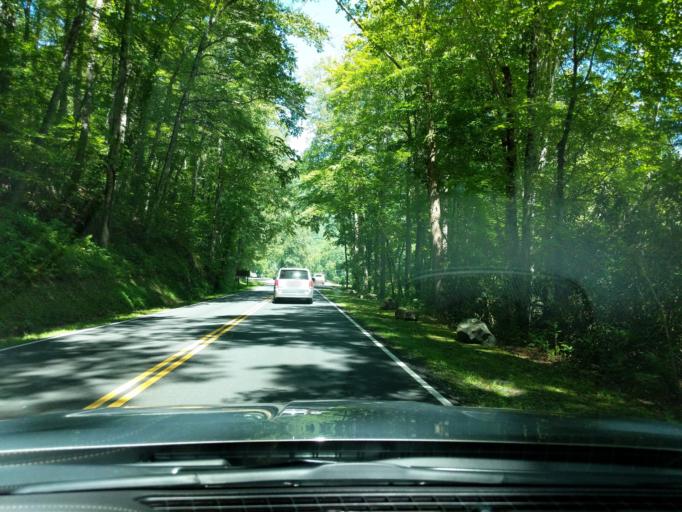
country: US
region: North Carolina
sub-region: Swain County
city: Cherokee
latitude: 35.5234
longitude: -83.3065
